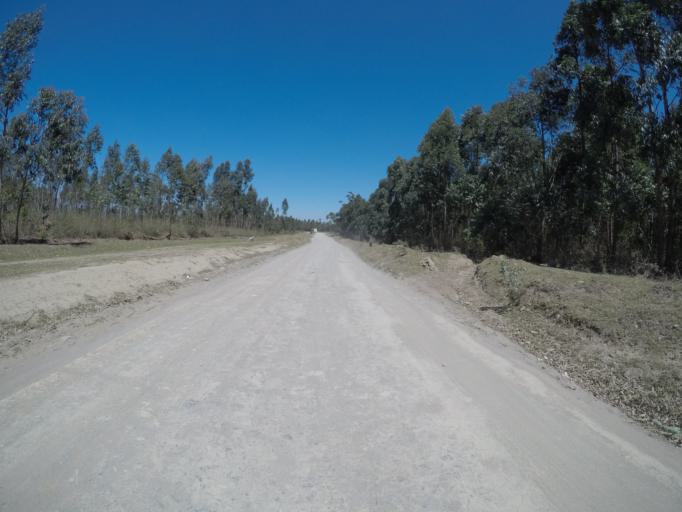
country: ZA
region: Eastern Cape
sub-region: OR Tambo District Municipality
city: Libode
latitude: -31.9509
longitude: 29.0243
